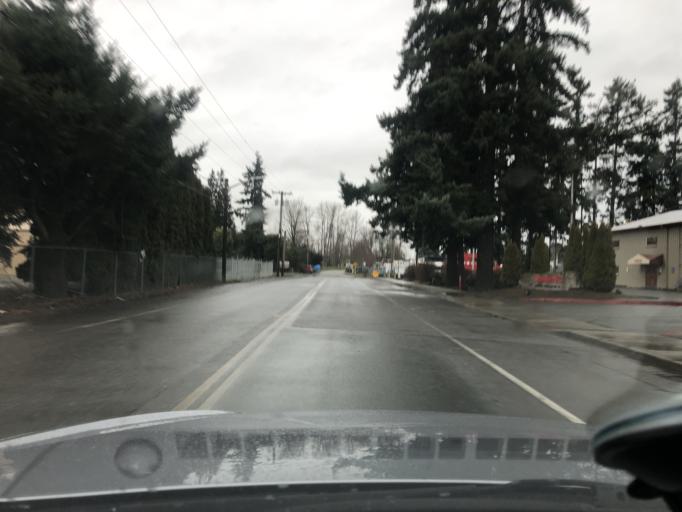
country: US
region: Washington
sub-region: King County
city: Kent
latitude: 47.3651
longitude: -122.2350
